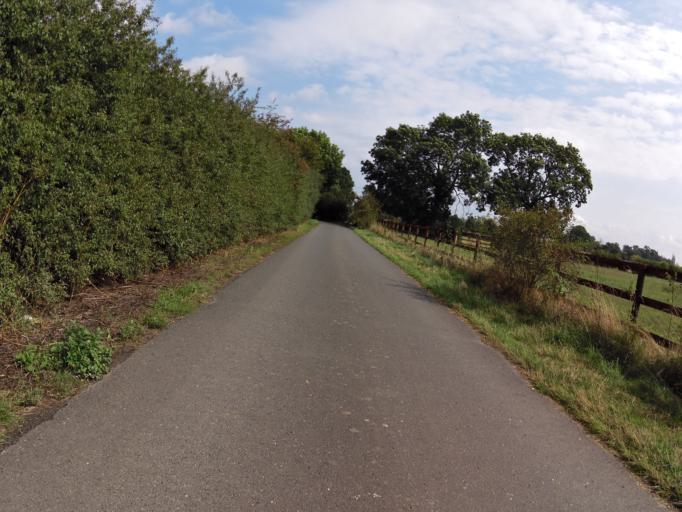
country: DE
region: Lower Saxony
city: Hoya
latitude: 52.7930
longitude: 9.1400
